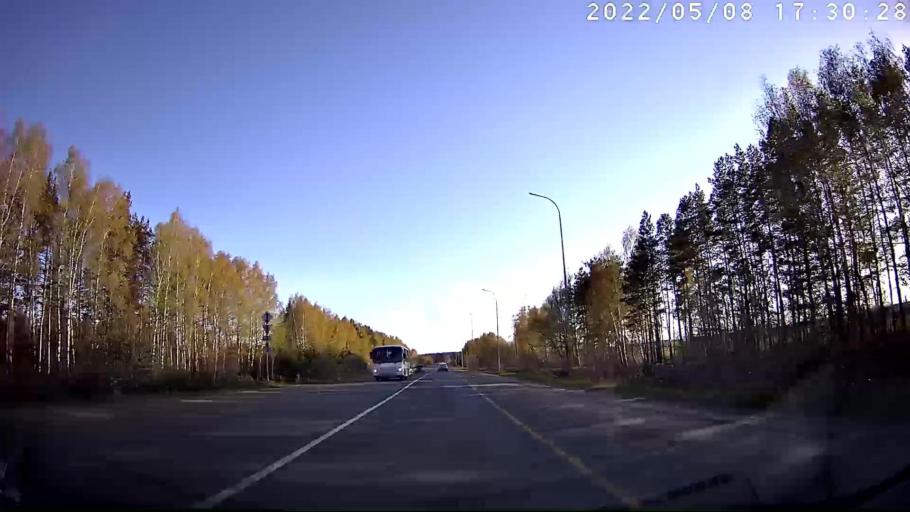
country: RU
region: Mariy-El
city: Volzhsk
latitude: 55.9098
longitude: 48.3628
